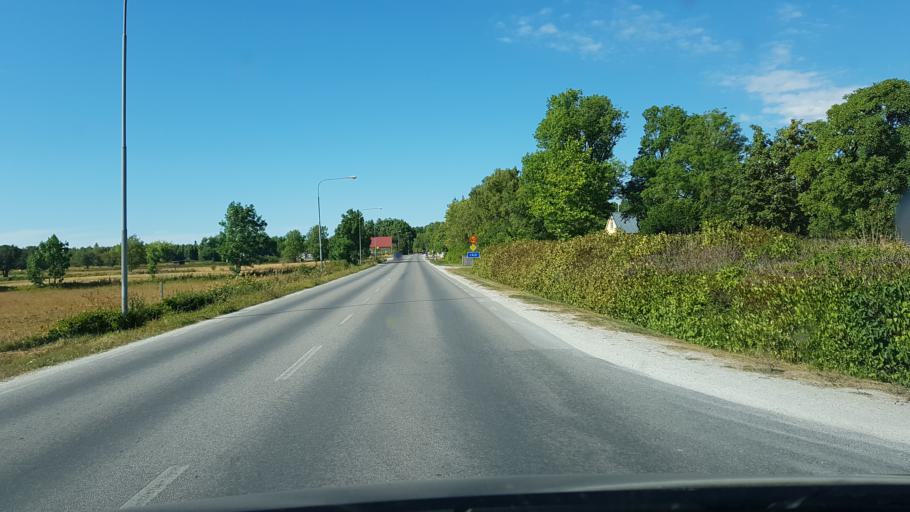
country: SE
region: Gotland
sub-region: Gotland
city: Klintehamn
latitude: 57.4403
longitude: 18.1451
